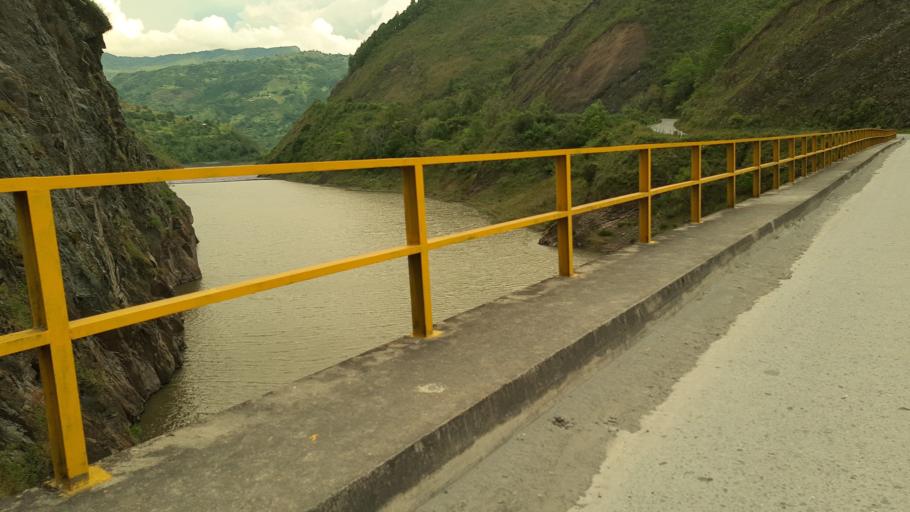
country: CO
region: Boyaca
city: Somondoco
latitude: 5.0168
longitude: -73.3859
